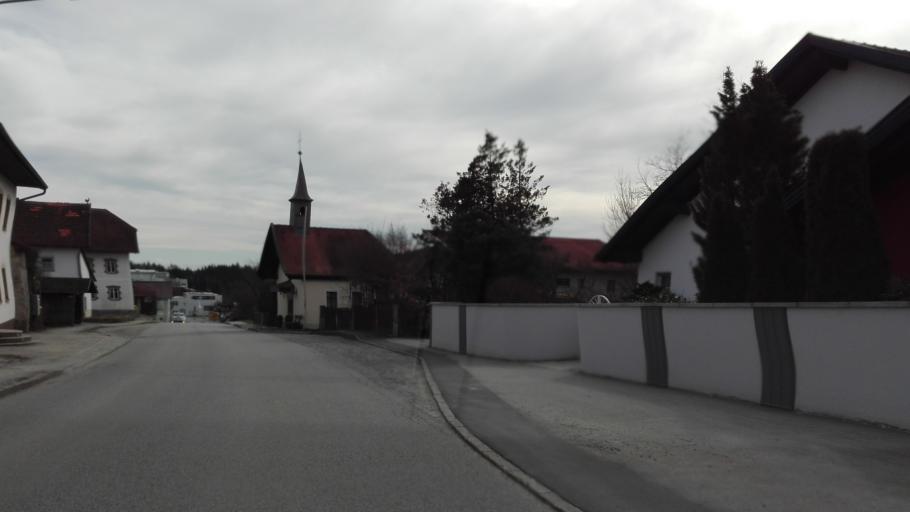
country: DE
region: Bavaria
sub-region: Lower Bavaria
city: Hauzenberg
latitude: 48.6326
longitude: 13.6425
